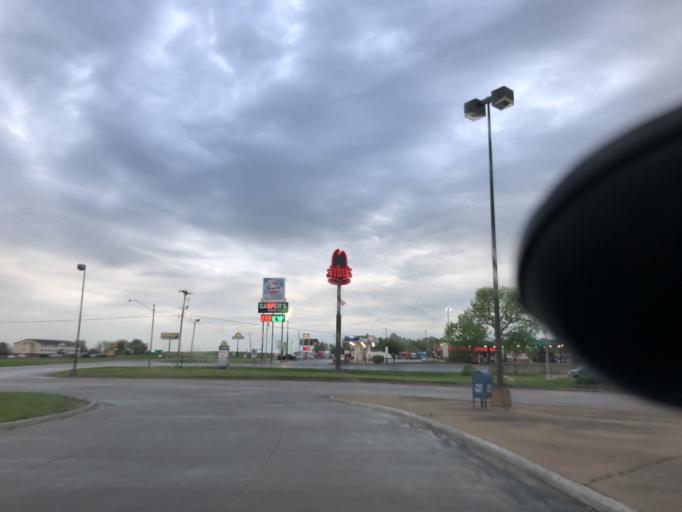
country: US
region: Missouri
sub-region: Callaway County
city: Fulton
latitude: 38.9418
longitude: -91.9426
